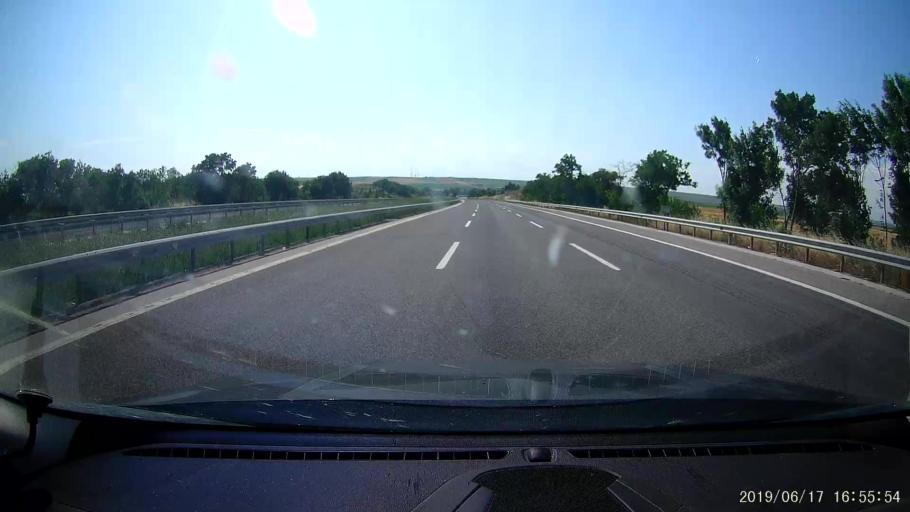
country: TR
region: Edirne
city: Haskoy
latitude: 41.5825
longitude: 26.9523
